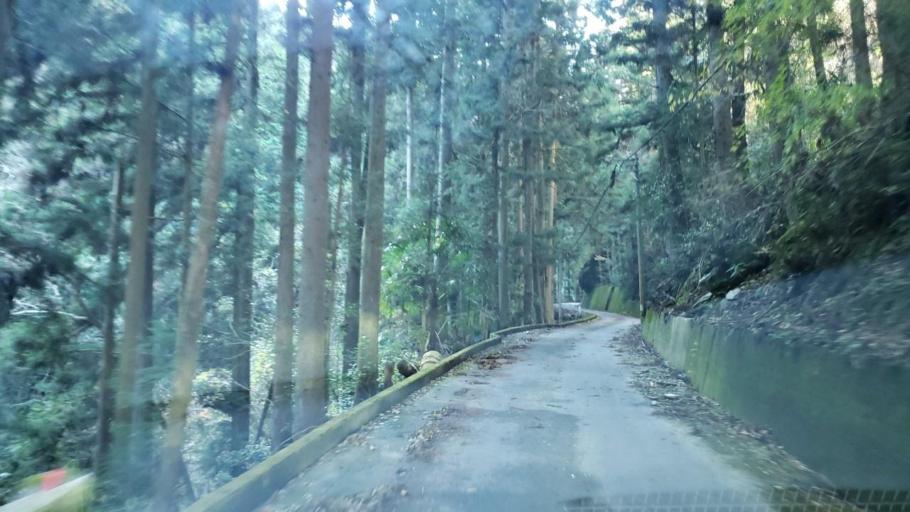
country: JP
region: Tokushima
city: Wakimachi
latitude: 33.9896
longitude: 133.9949
